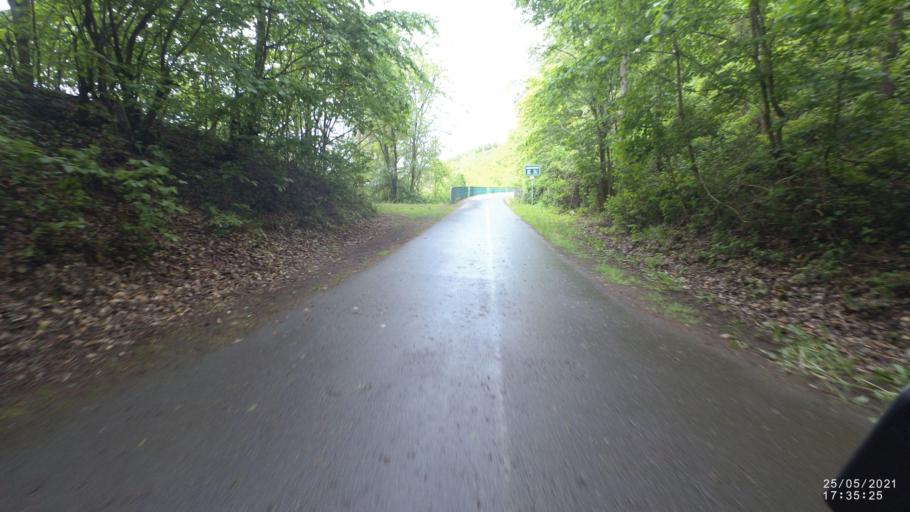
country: DE
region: Rheinland-Pfalz
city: Trimbs
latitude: 50.3164
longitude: 7.2782
